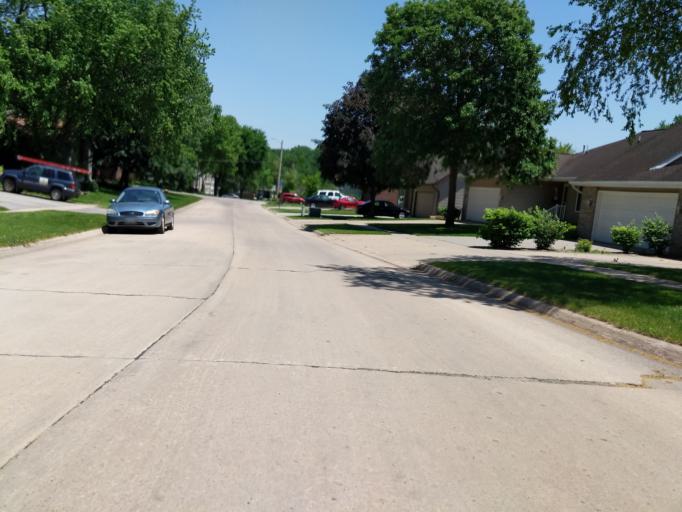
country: US
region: Iowa
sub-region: Linn County
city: Cedar Rapids
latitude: 42.0180
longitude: -91.6290
